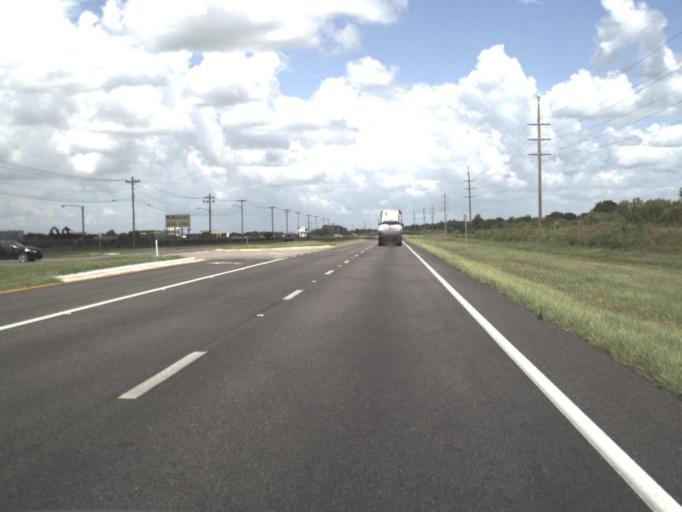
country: US
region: Florida
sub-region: Polk County
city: Bartow
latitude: 27.8392
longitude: -81.8238
